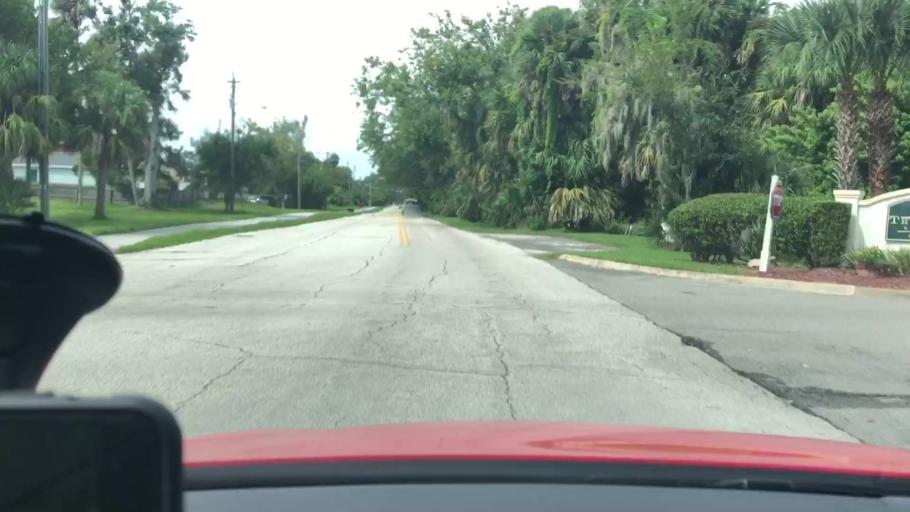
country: US
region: Florida
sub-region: Volusia County
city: South Daytona
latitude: 29.1865
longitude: -81.0082
